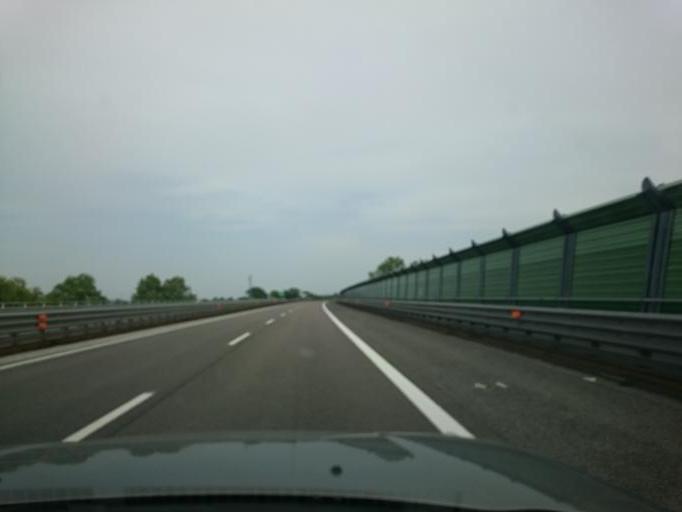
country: IT
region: Veneto
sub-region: Provincia di Venezia
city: Dese
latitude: 45.5343
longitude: 12.3009
